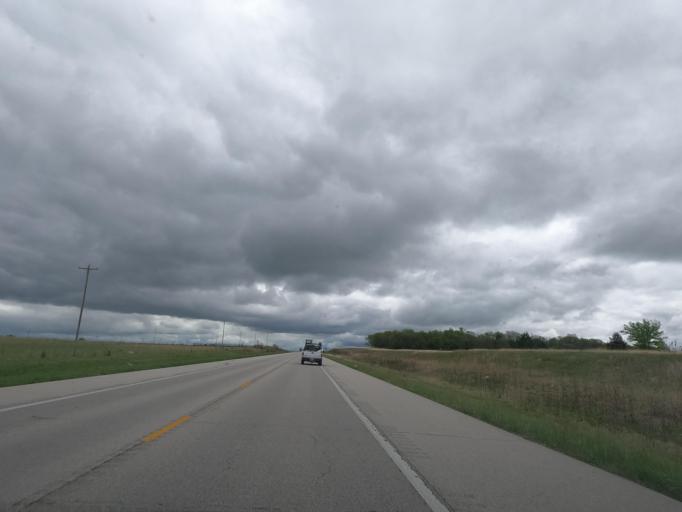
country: US
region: Kansas
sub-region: Wilson County
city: Fredonia
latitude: 37.5015
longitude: -95.7729
